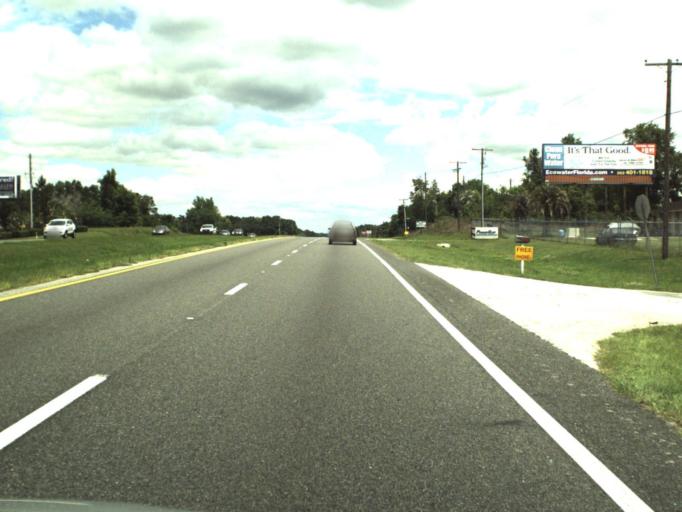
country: US
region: Florida
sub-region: Marion County
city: Ocala
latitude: 29.2530
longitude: -82.1520
